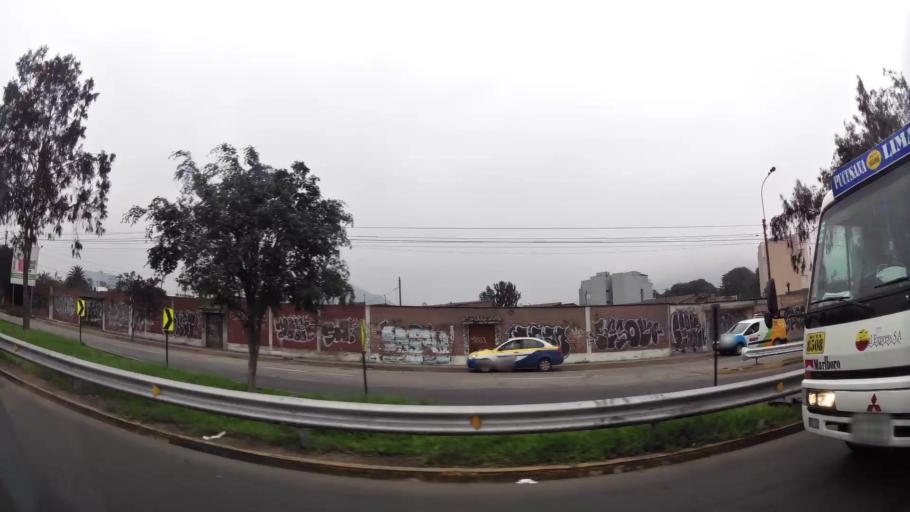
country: PE
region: Lima
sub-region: Lima
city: San Luis
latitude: -12.1062
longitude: -76.9787
